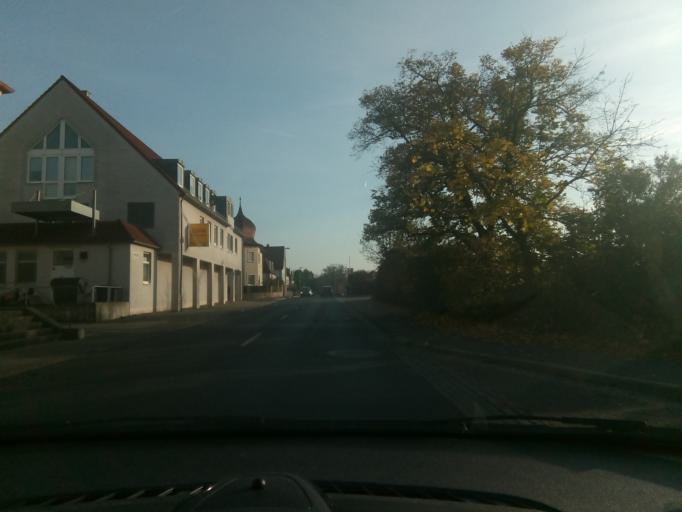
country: DE
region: Bavaria
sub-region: Regierungsbezirk Unterfranken
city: Gerolzhofen
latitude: 49.9009
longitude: 10.3436
